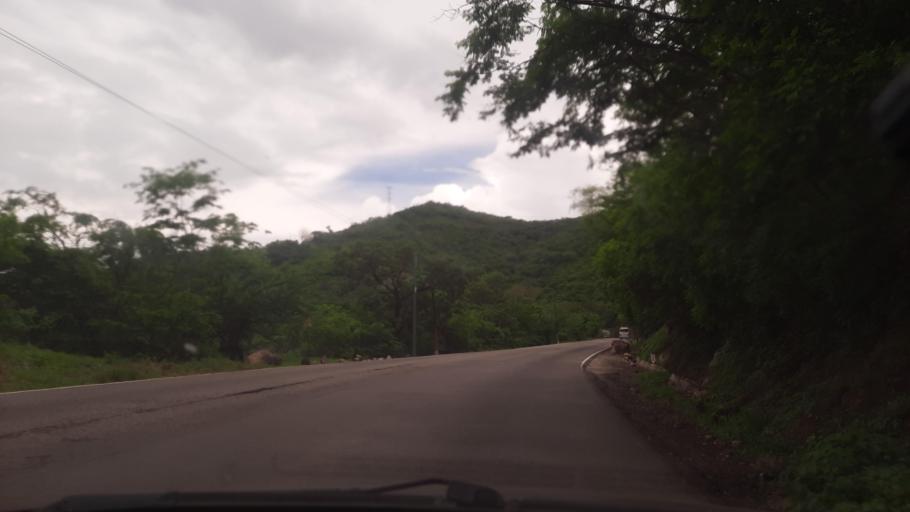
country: GT
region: Zacapa
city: San Jorge
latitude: 14.8805
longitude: -89.5153
